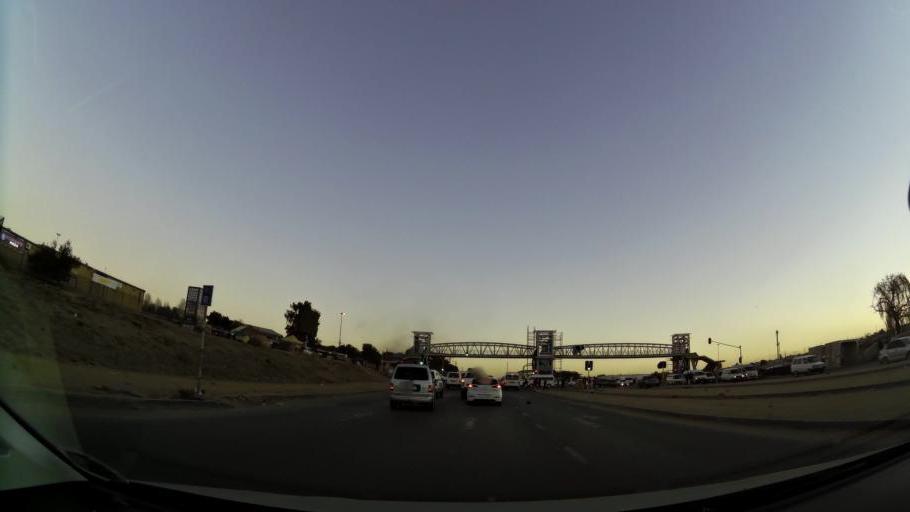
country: ZA
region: Gauteng
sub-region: Ekurhuleni Metropolitan Municipality
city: Tembisa
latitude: -26.0271
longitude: 28.1949
